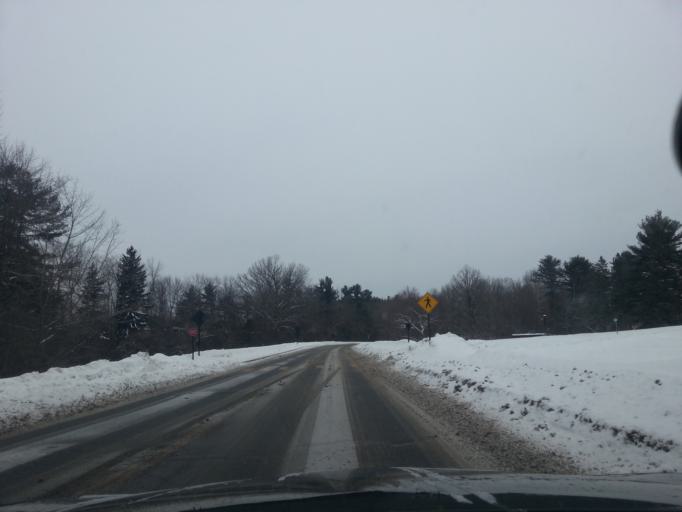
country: CA
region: Ontario
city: Ottawa
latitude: 45.4233
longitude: -75.7450
